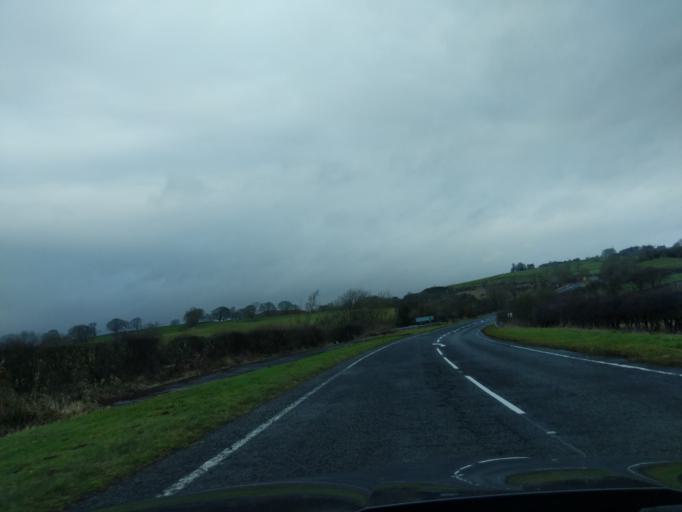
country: GB
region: England
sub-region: Northumberland
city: Rothley
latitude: 55.1534
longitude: -2.0113
